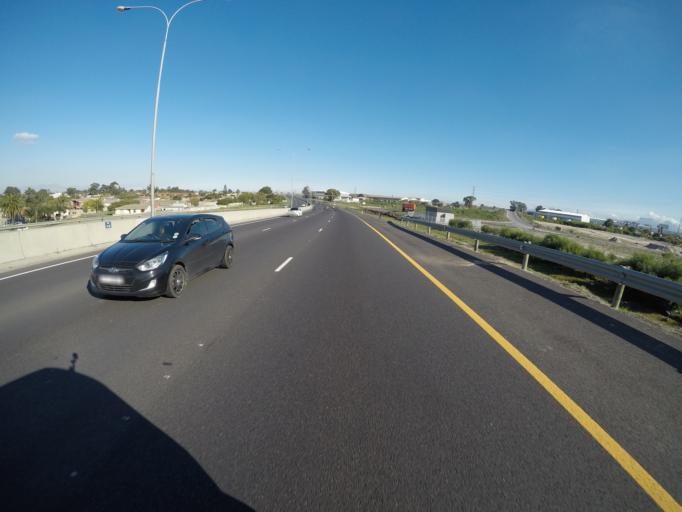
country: ZA
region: Western Cape
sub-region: City of Cape Town
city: Kraaifontein
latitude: -33.9211
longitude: 18.6644
